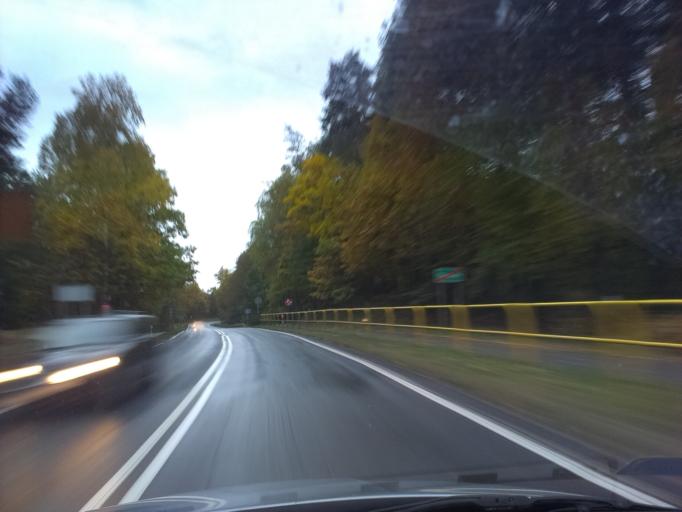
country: PL
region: Kujawsko-Pomorskie
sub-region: Powiat tucholski
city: Tuchola
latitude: 53.5619
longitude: 17.9010
